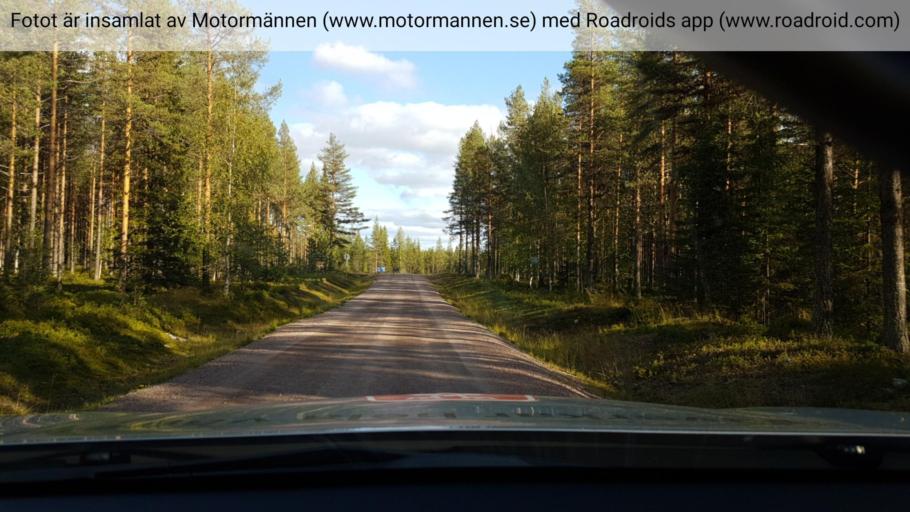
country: SE
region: Vaesterbotten
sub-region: Mala Kommun
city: Mala
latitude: 65.2584
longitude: 18.5888
